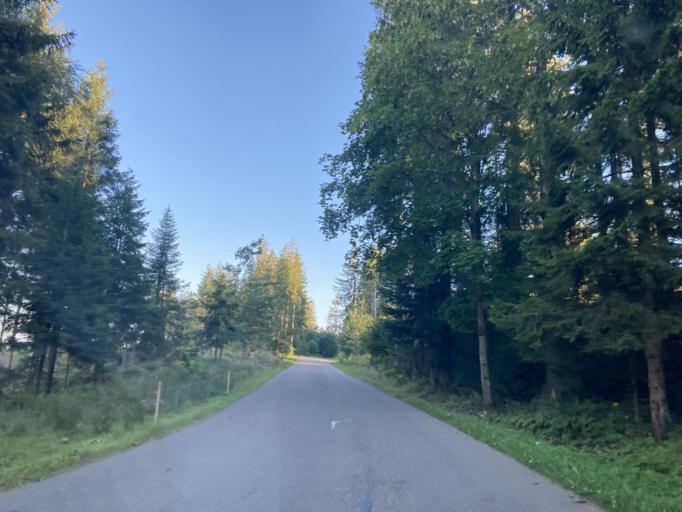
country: DE
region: Baden-Wuerttemberg
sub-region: Freiburg Region
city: Schonach im Schwarzwald
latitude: 48.1662
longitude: 8.1859
